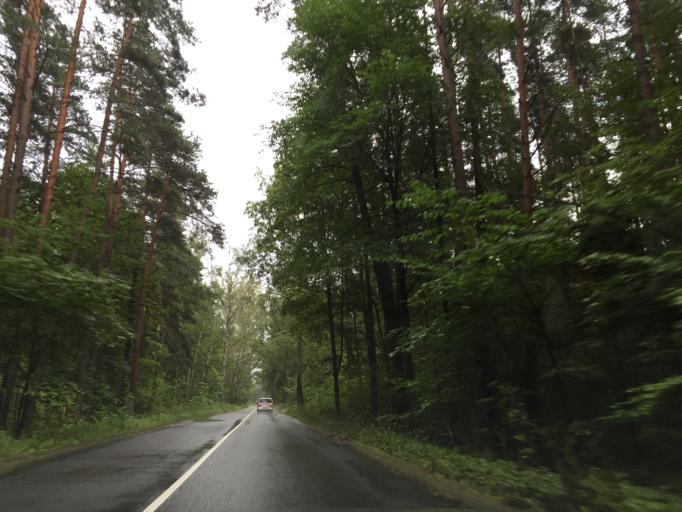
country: LV
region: Babite
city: Pinki
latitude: 56.9558
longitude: 23.9654
